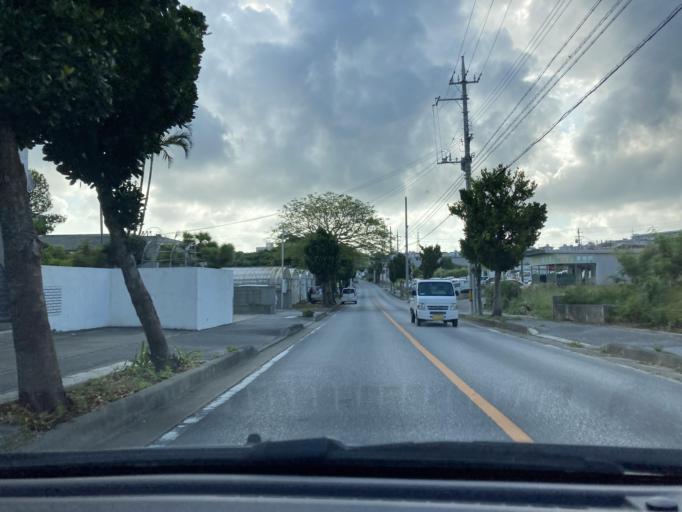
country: JP
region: Okinawa
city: Tomigusuku
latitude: 26.1756
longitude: 127.7197
